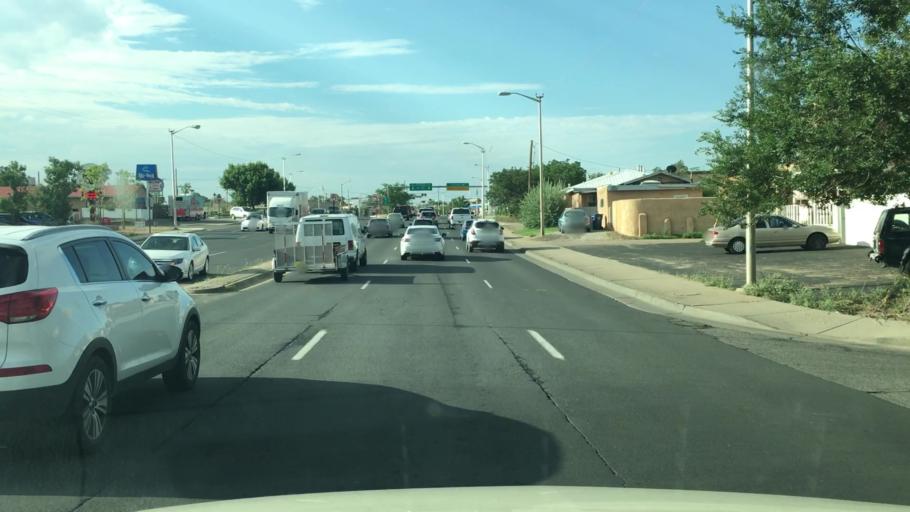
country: US
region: New Mexico
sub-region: Santa Fe County
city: Santa Fe
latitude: 35.6800
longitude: -105.9545
